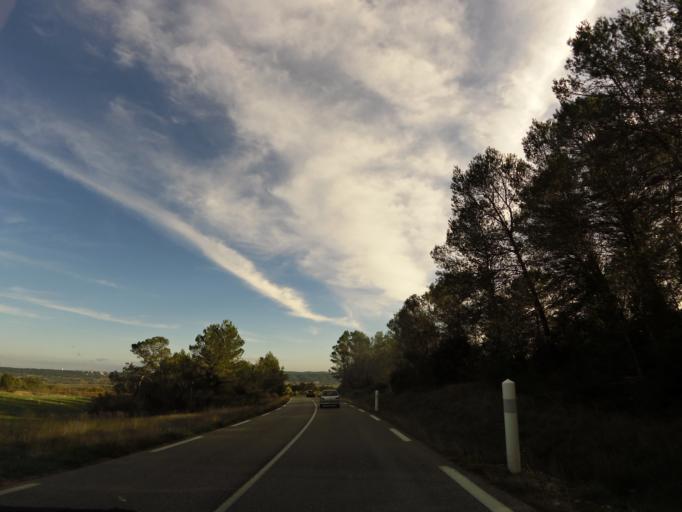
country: FR
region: Languedoc-Roussillon
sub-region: Departement du Gard
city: Ledignan
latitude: 43.9544
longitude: 4.0998
